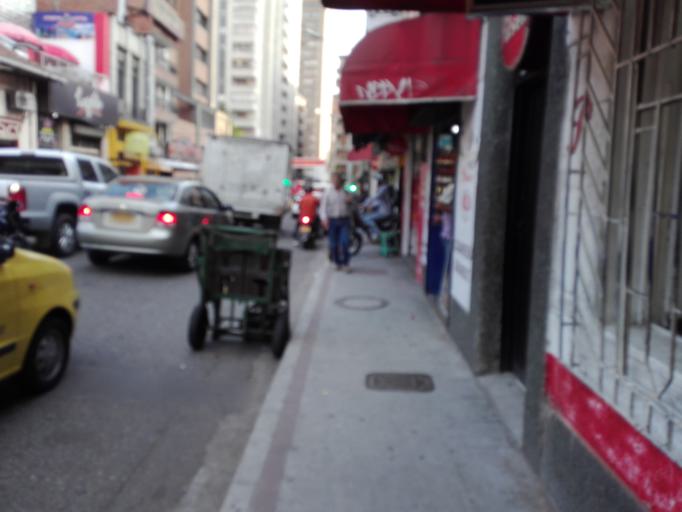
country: CO
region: Antioquia
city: Medellin
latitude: 6.2489
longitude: -75.5621
